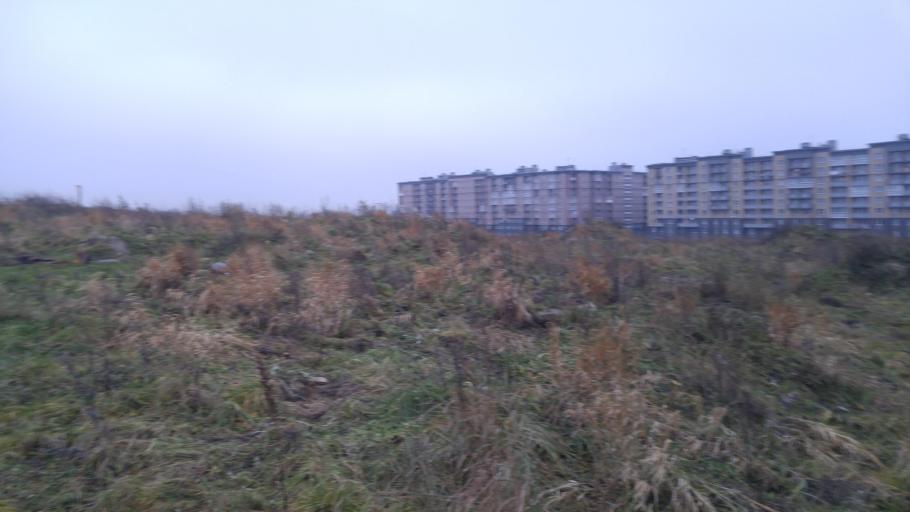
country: RU
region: St.-Petersburg
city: Tyarlevo
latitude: 59.7469
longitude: 30.4854
